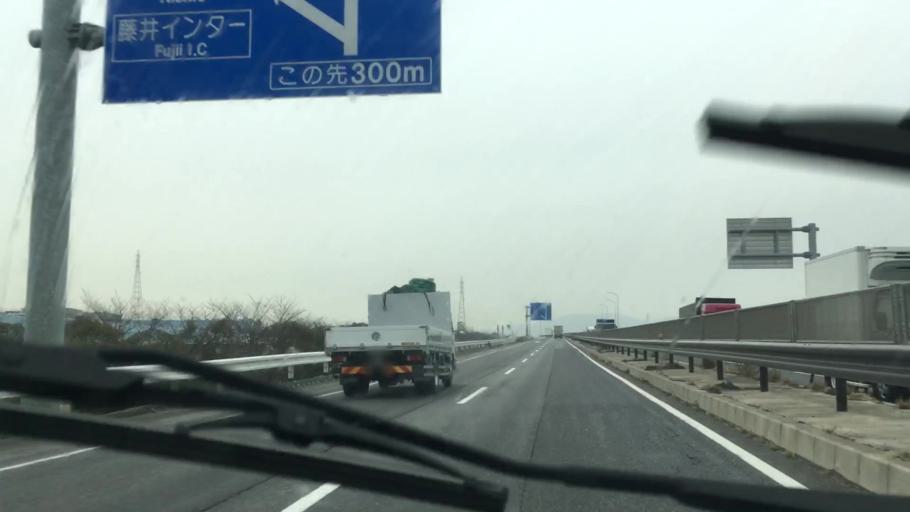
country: JP
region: Aichi
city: Nishio
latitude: 34.9032
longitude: 137.0667
